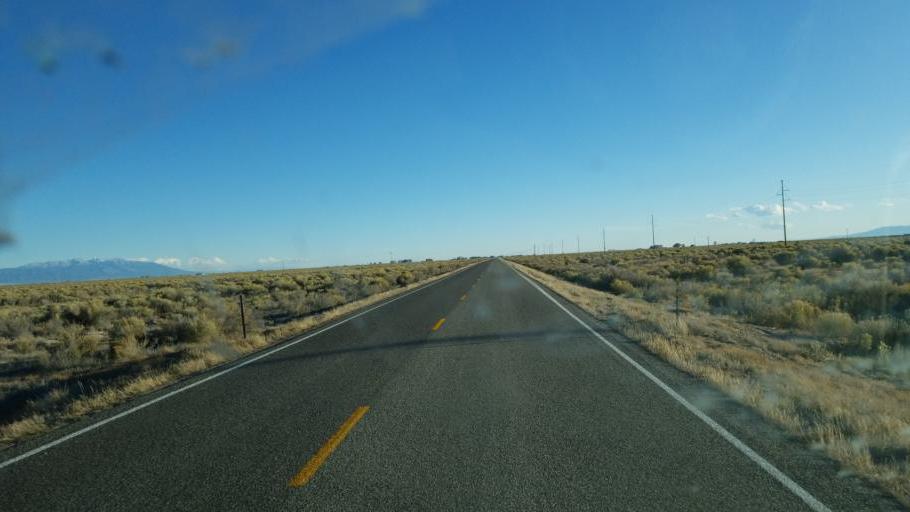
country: US
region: Colorado
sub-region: Saguache County
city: Saguache
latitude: 38.0758
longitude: -105.9170
